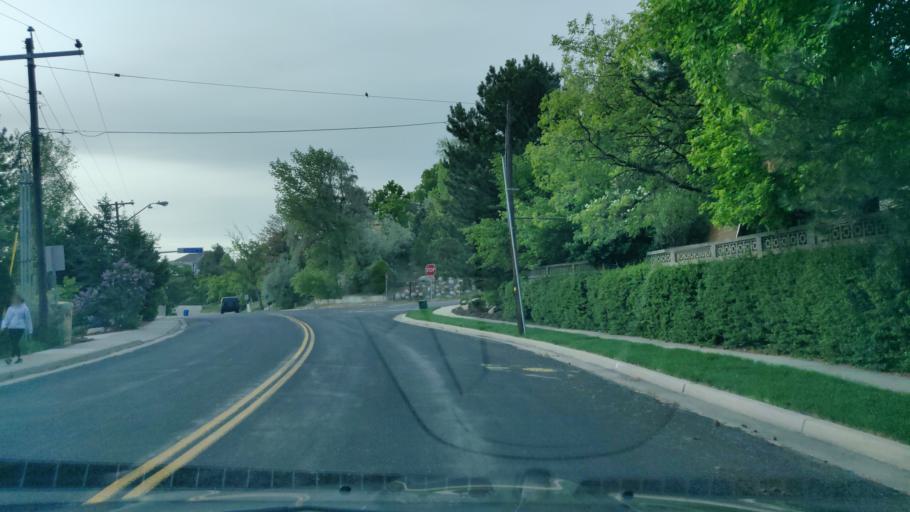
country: US
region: Utah
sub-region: Salt Lake County
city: Cottonwood Heights
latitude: 40.6042
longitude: -111.8049
